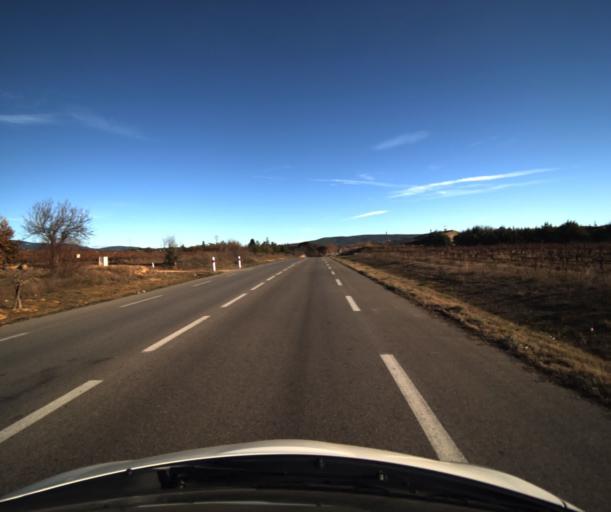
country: FR
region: Provence-Alpes-Cote d'Azur
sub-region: Departement du Vaucluse
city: Pertuis
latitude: 43.7142
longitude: 5.5282
